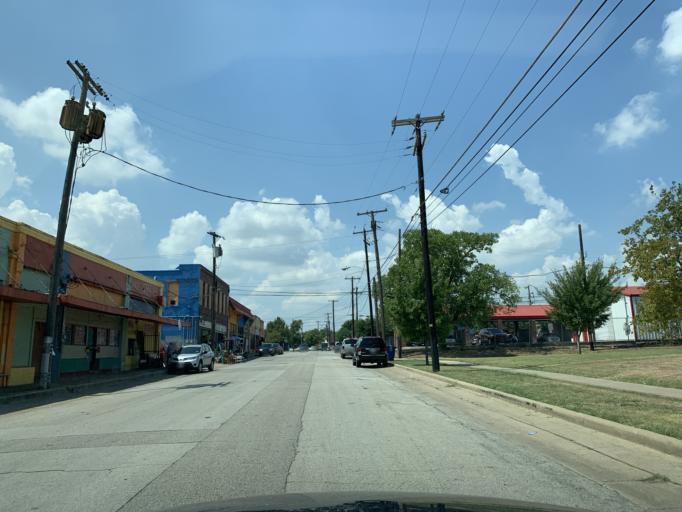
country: US
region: Texas
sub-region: Dallas County
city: Dallas
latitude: 32.7483
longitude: -96.8144
